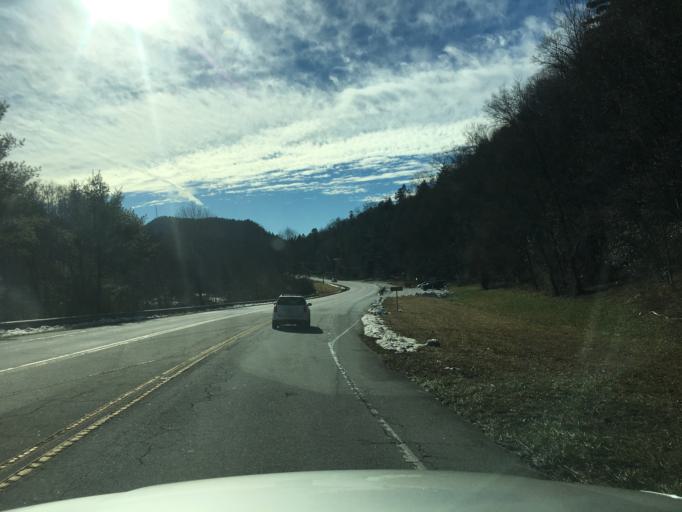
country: US
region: North Carolina
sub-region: Transylvania County
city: Brevard
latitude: 35.1485
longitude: -82.8320
